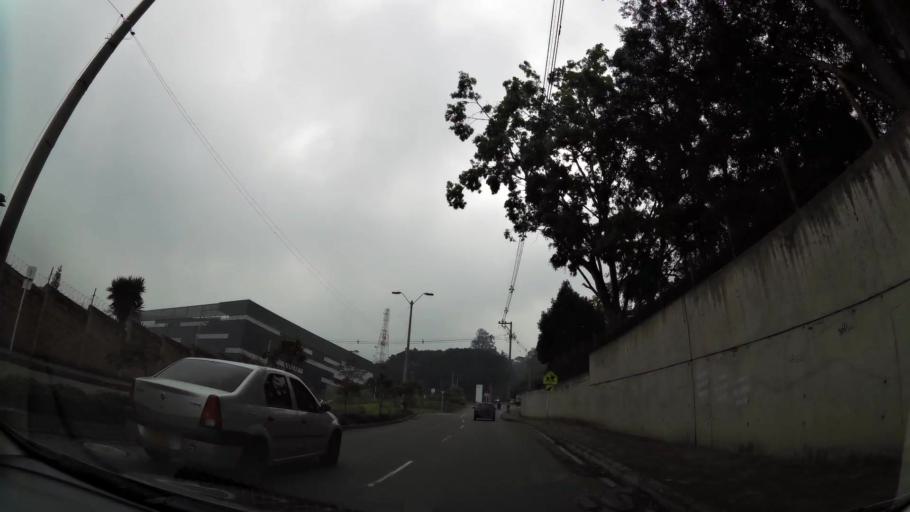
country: CO
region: Antioquia
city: Envigado
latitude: 6.1870
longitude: -75.5607
